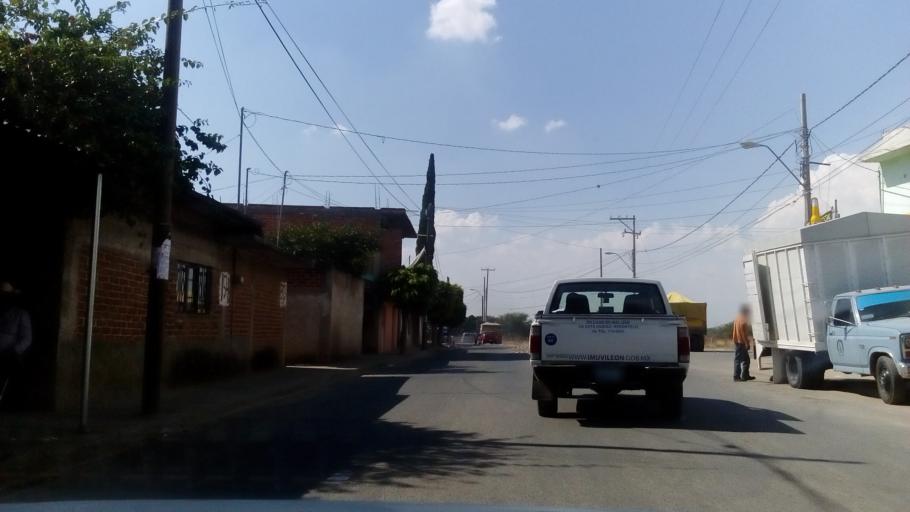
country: MX
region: Guanajuato
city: Duarte
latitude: 21.0883
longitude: -101.5276
